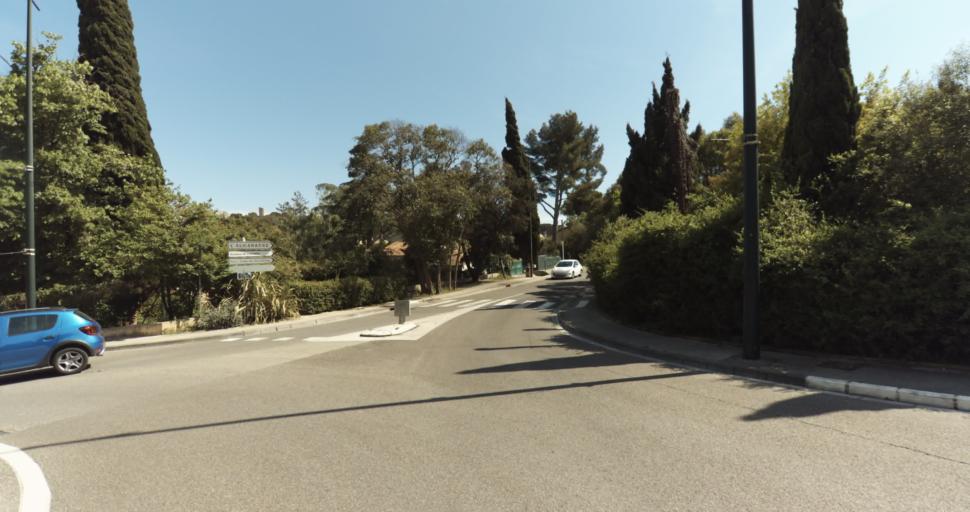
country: FR
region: Provence-Alpes-Cote d'Azur
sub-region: Departement du Var
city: Hyeres
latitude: 43.1031
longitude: 6.1213
